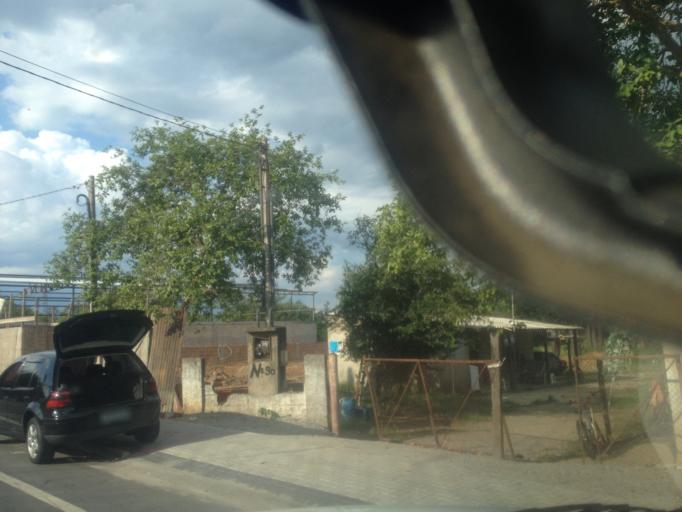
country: BR
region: Rio de Janeiro
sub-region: Porto Real
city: Porto Real
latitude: -22.4497
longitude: -44.3025
